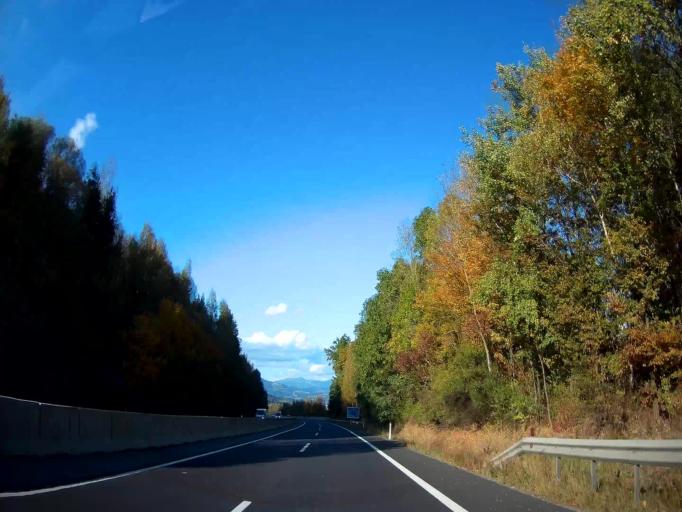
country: AT
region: Carinthia
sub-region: Politischer Bezirk Wolfsberg
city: Sankt Andrae
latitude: 46.7533
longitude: 14.8162
